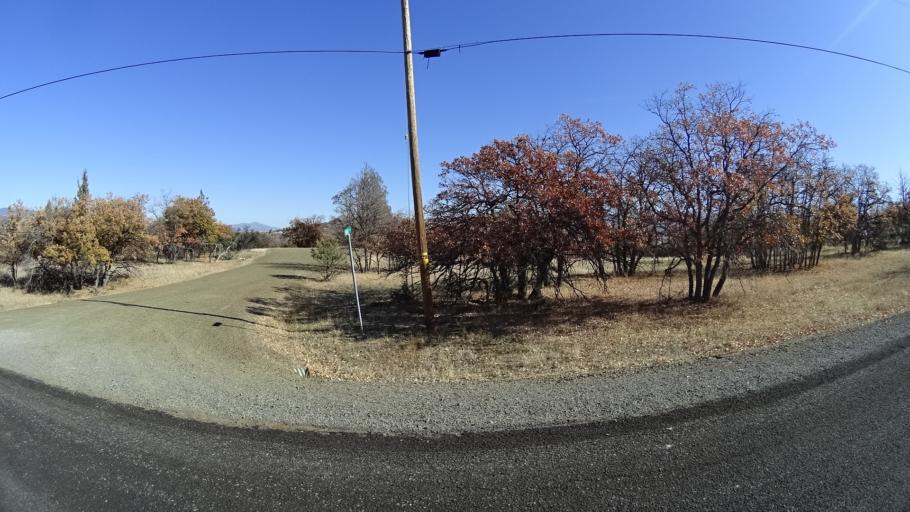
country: US
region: California
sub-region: Siskiyou County
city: Montague
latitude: 41.8805
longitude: -122.4890
